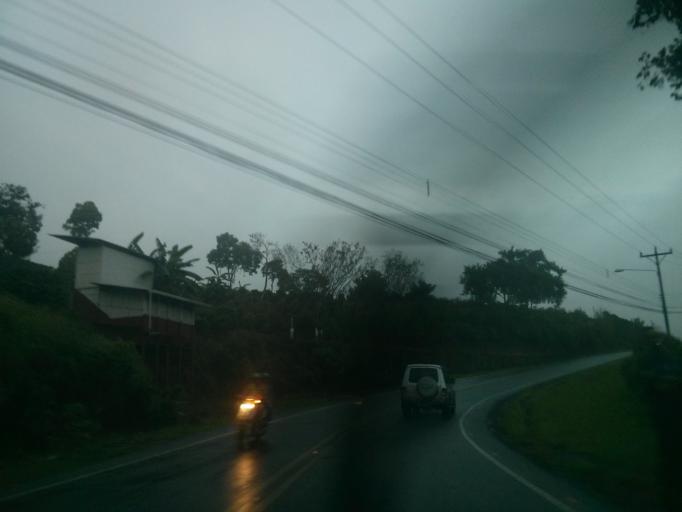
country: CR
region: Alajuela
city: Alajuela
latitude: 10.0447
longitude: -84.2093
